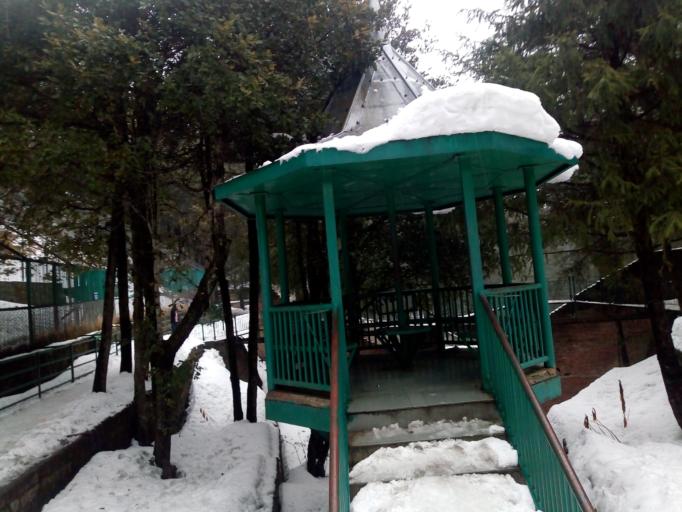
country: IN
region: Himachal Pradesh
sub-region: Shimla
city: Shimla
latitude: 31.0958
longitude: 77.2632
